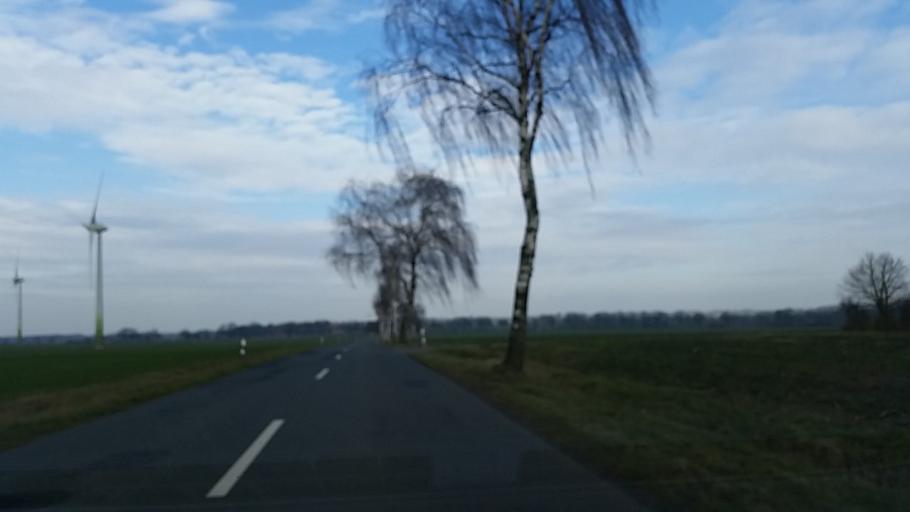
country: DE
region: Lower Saxony
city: Romstedt
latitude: 53.1226
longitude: 10.6402
